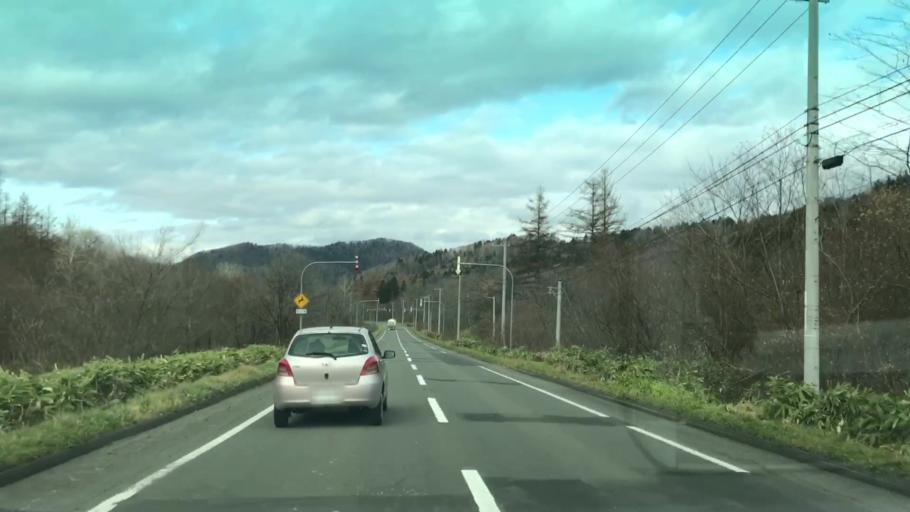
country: JP
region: Hokkaido
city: Shimo-furano
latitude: 42.9362
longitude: 142.4450
